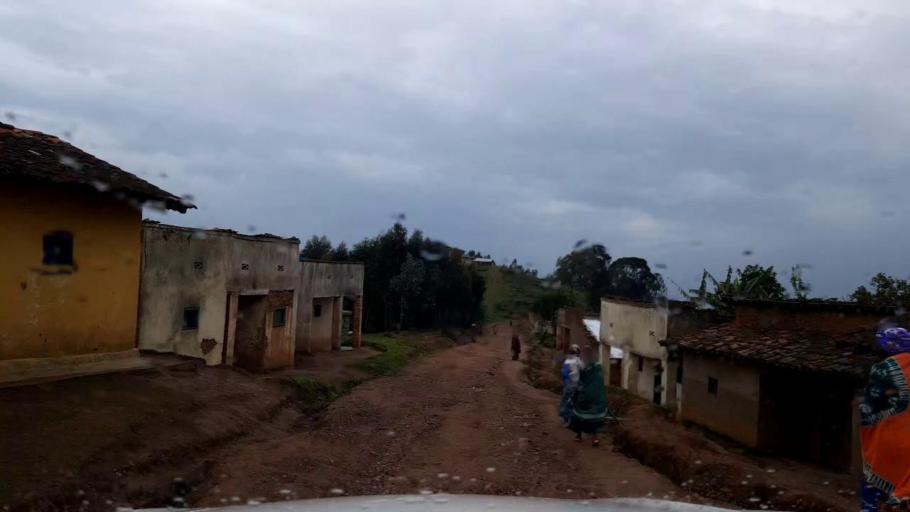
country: RW
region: Western Province
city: Kibuye
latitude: -2.0220
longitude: 29.4601
